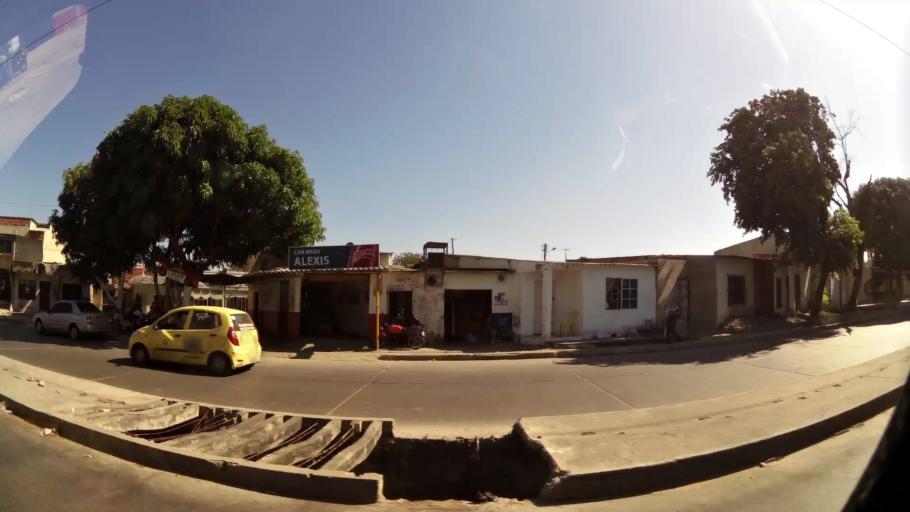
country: CO
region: Atlantico
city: Soledad
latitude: 10.9296
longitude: -74.7914
